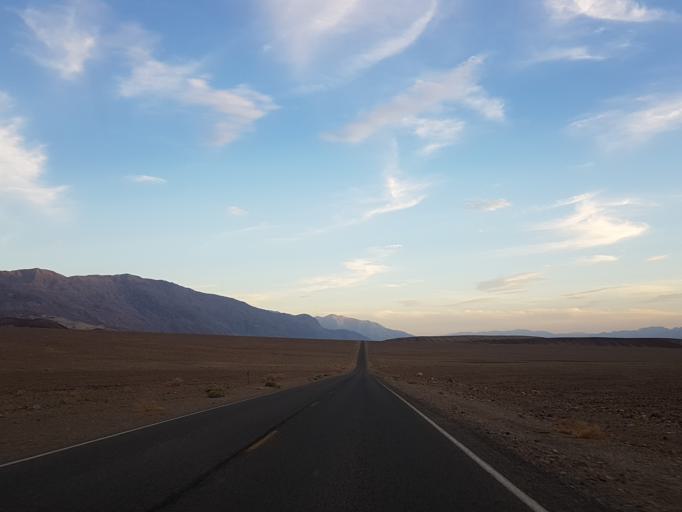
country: US
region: Nevada
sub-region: Nye County
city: Beatty
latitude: 36.3519
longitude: -116.8393
